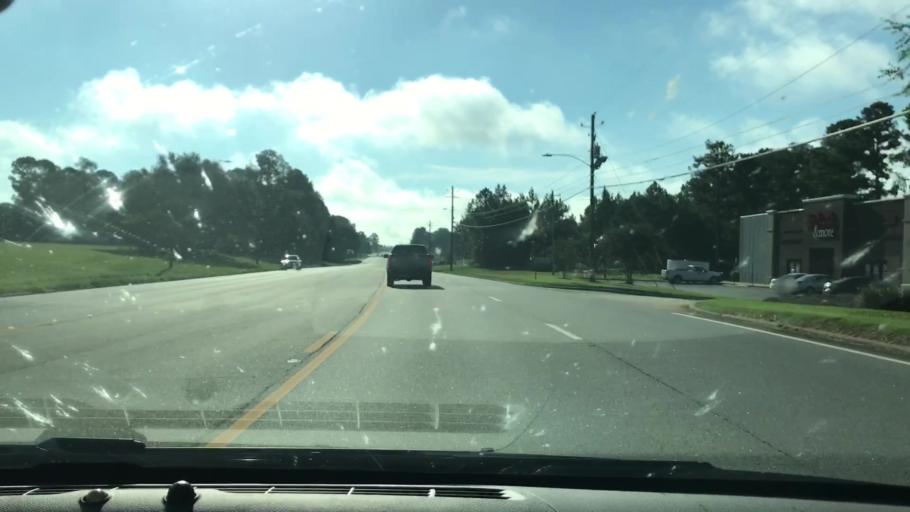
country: US
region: Georgia
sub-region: Terrell County
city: Dawson
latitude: 31.7634
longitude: -84.4441
